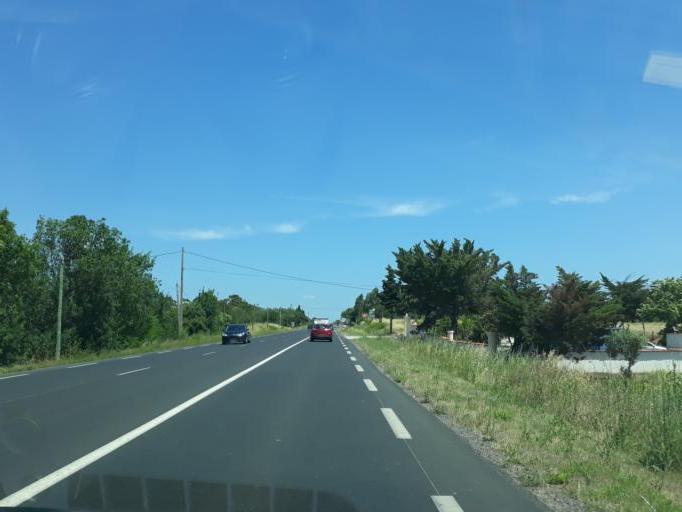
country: FR
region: Languedoc-Roussillon
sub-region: Departement de l'Herault
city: Portiragnes
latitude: 43.3145
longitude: 3.3713
